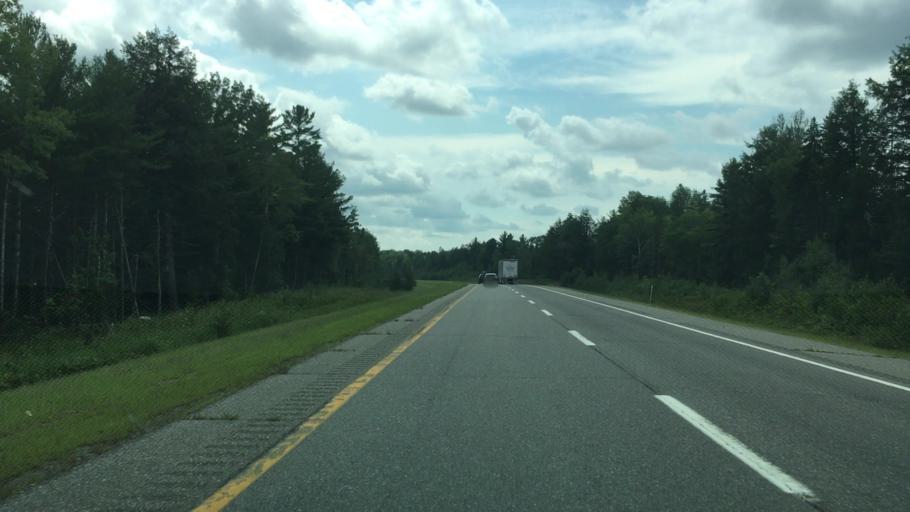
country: US
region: Maine
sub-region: Penobscot County
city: Howland
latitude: 45.3183
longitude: -68.6532
